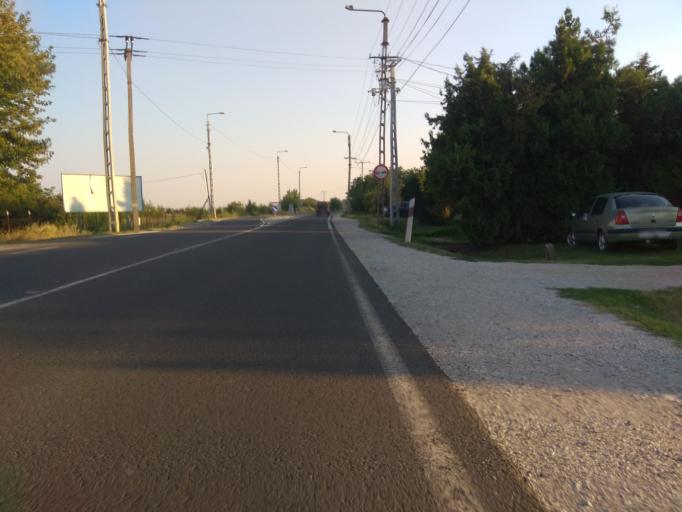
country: HU
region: Borsod-Abauj-Zemplen
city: Nyekladhaza
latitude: 47.9851
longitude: 20.8314
